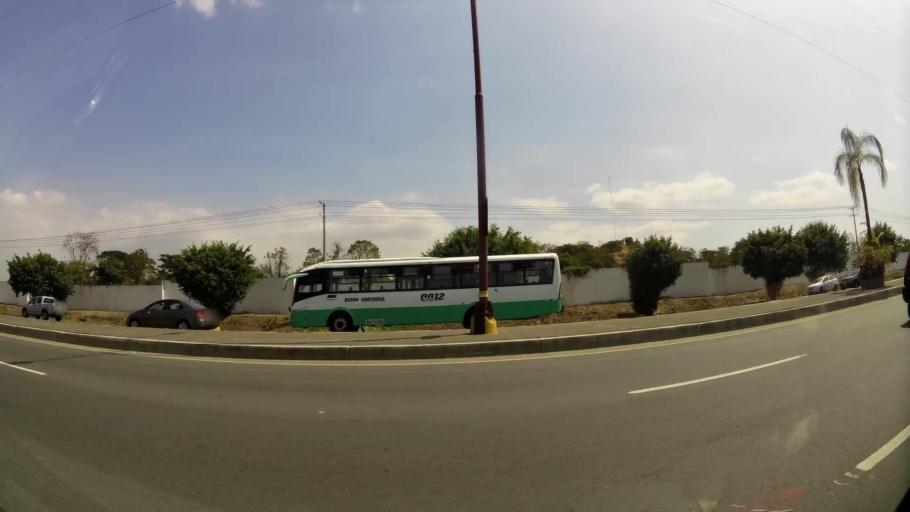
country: EC
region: Guayas
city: Eloy Alfaro
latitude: -2.0823
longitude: -79.8735
